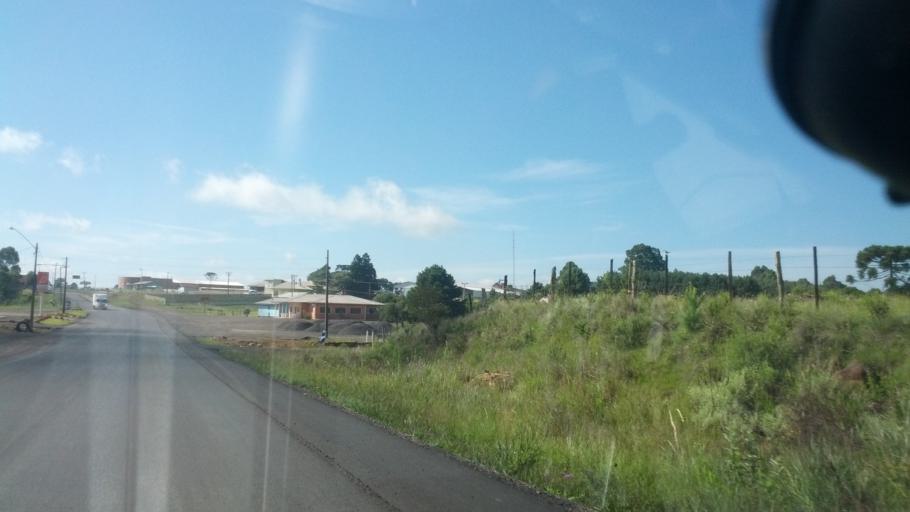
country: BR
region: Santa Catarina
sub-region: Lages
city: Lages
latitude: -27.9407
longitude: -50.5103
